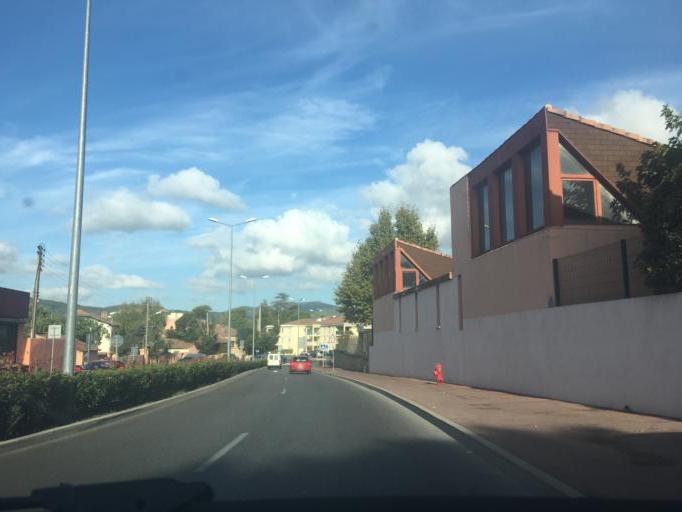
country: FR
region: Provence-Alpes-Cote d'Azur
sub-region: Departement du Var
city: Draguignan
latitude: 43.5338
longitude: 6.4633
